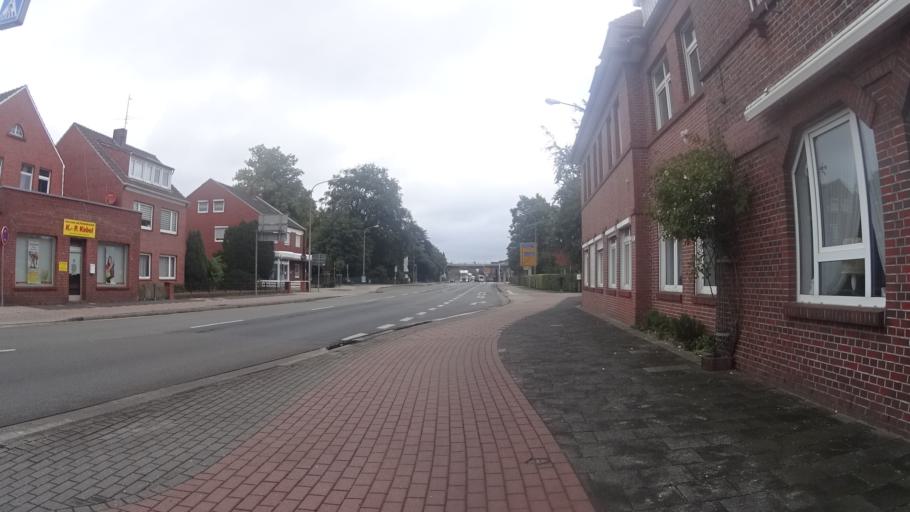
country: DE
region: Lower Saxony
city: Leer
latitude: 53.2377
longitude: 7.4555
